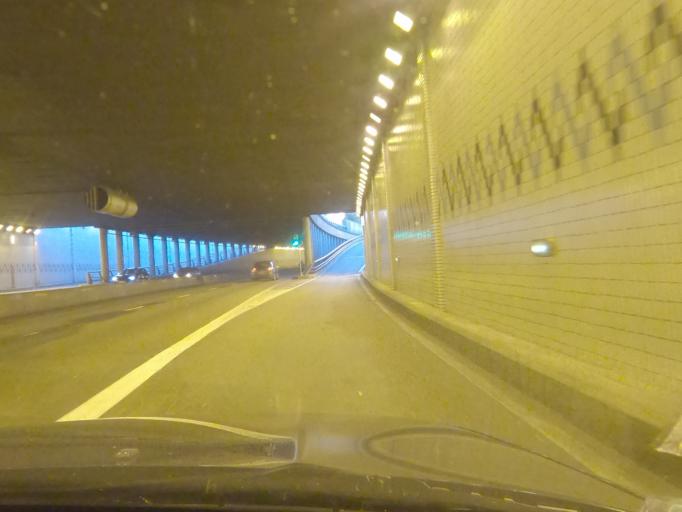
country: ES
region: Galicia
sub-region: Provincia de Pontevedra
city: Vigo
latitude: 42.2392
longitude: -8.7146
